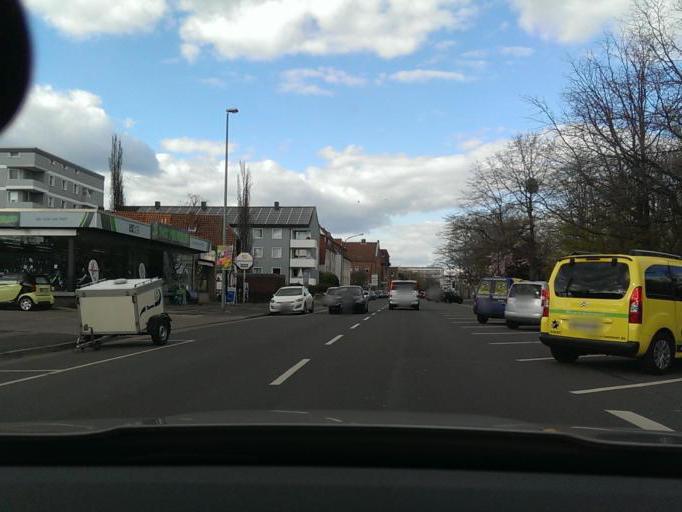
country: DE
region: Lower Saxony
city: Langenhagen
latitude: 52.4439
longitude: 9.7374
